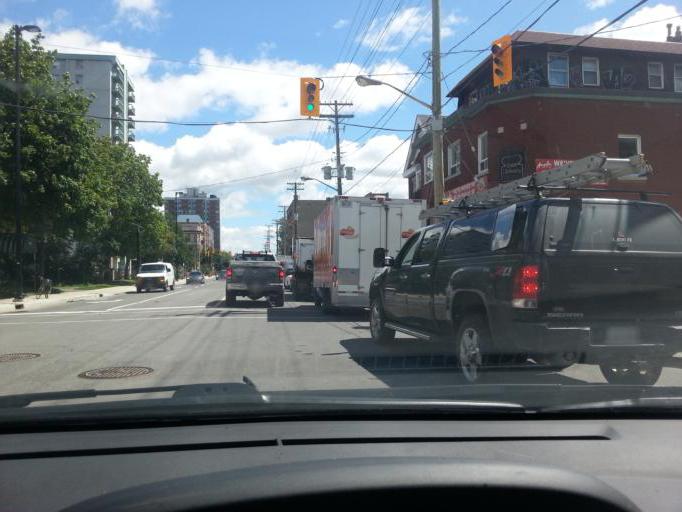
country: CA
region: Ontario
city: Ottawa
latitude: 45.4320
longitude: -75.6779
